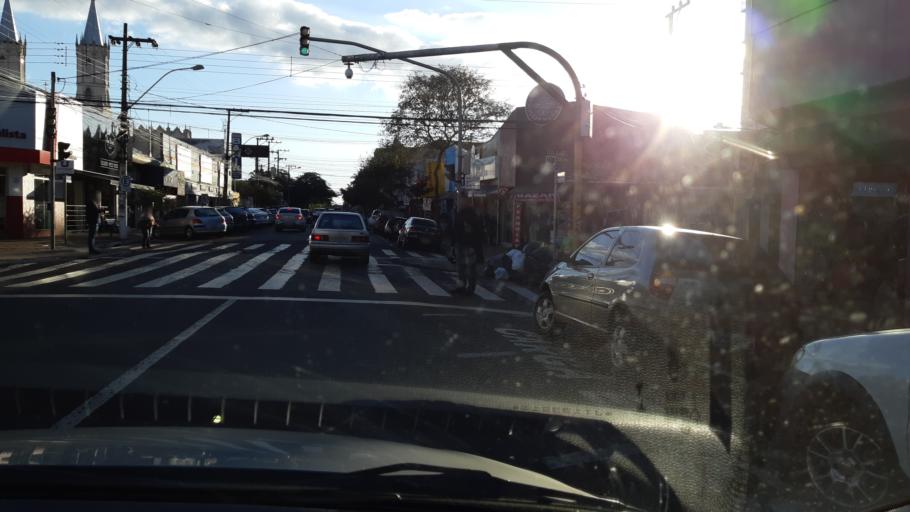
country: BR
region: Sao Paulo
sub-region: Ourinhos
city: Ourinhos
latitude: -22.9789
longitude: -49.8687
